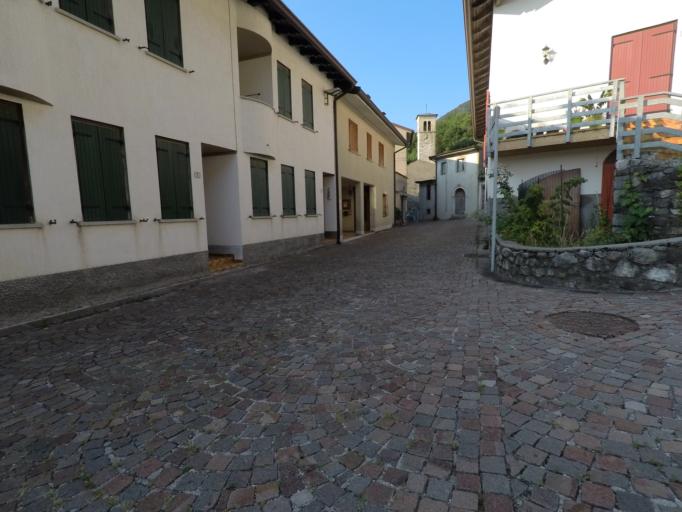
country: IT
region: Friuli Venezia Giulia
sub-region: Provincia di Udine
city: Trasaghis
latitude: 46.2584
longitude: 13.0388
